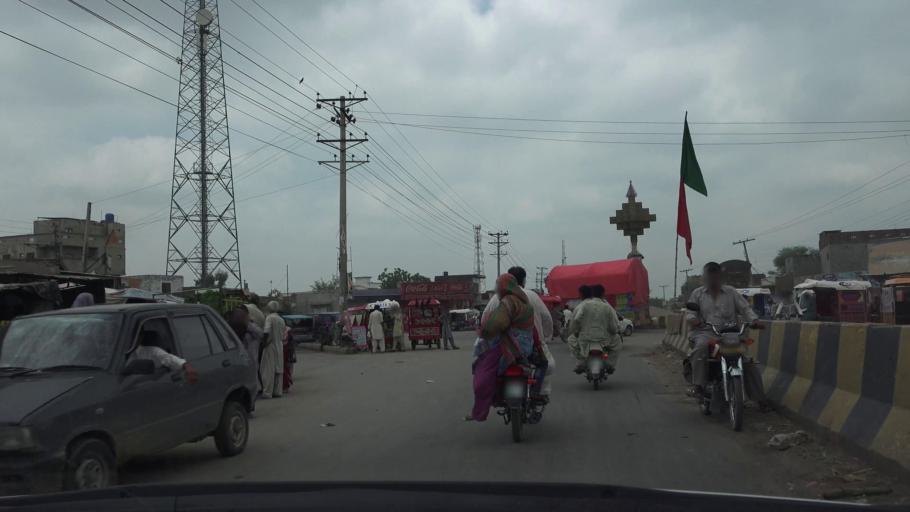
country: PK
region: Punjab
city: Faisalabad
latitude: 31.3876
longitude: 73.2005
